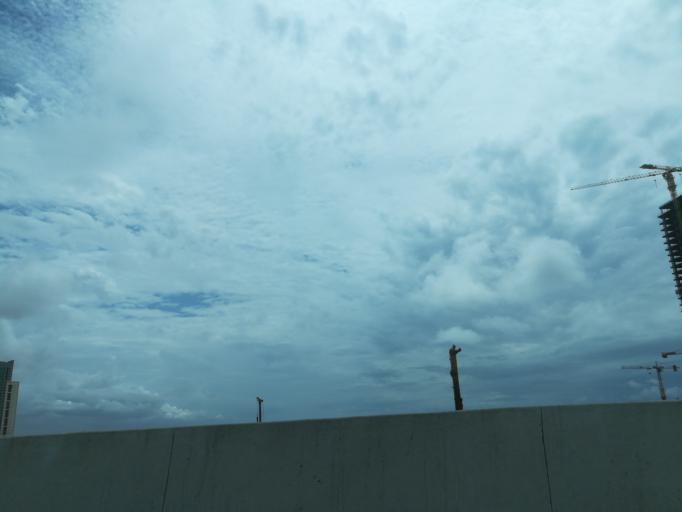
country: NG
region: Lagos
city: Lagos
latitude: 6.4051
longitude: 3.4038
